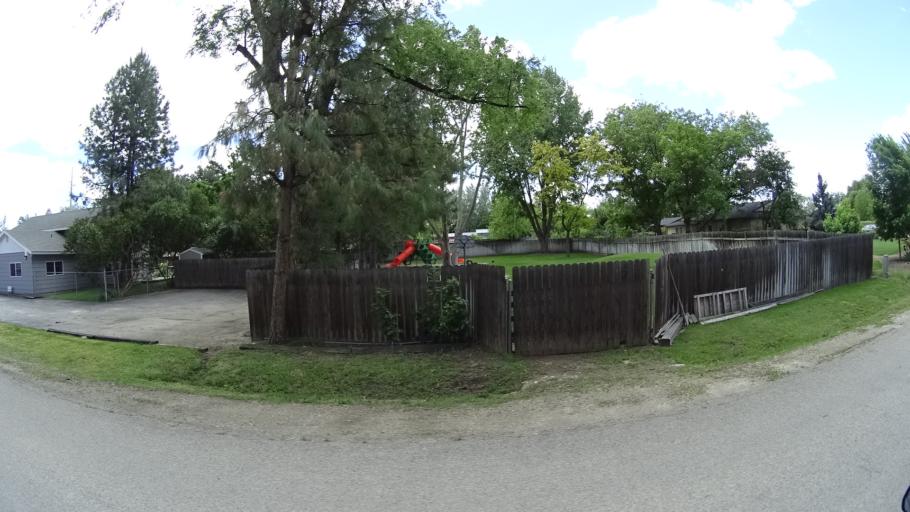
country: US
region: Idaho
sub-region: Ada County
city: Eagle
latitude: 43.6448
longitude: -116.3352
